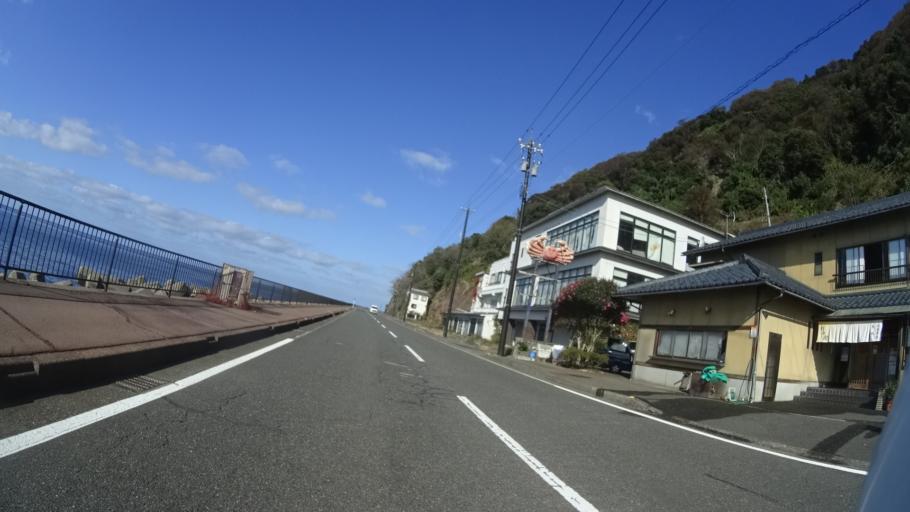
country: JP
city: Asahi
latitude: 35.8654
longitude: 136.0210
